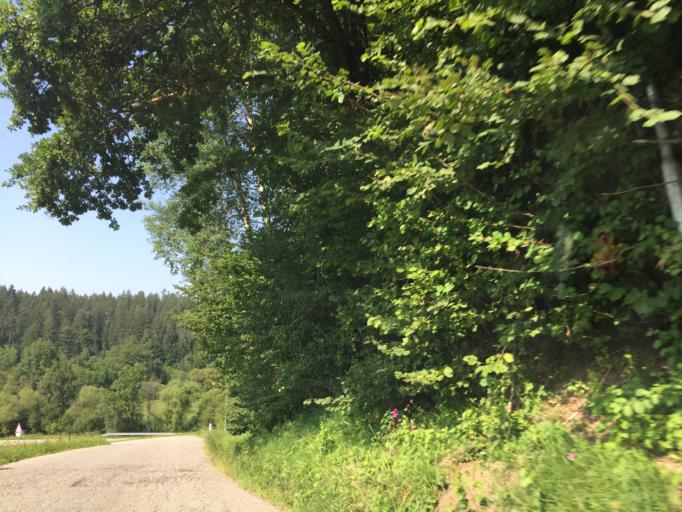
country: SI
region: Slovenj Gradec
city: Smartno pri Slovenj Gradcu
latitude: 46.4531
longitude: 15.1197
